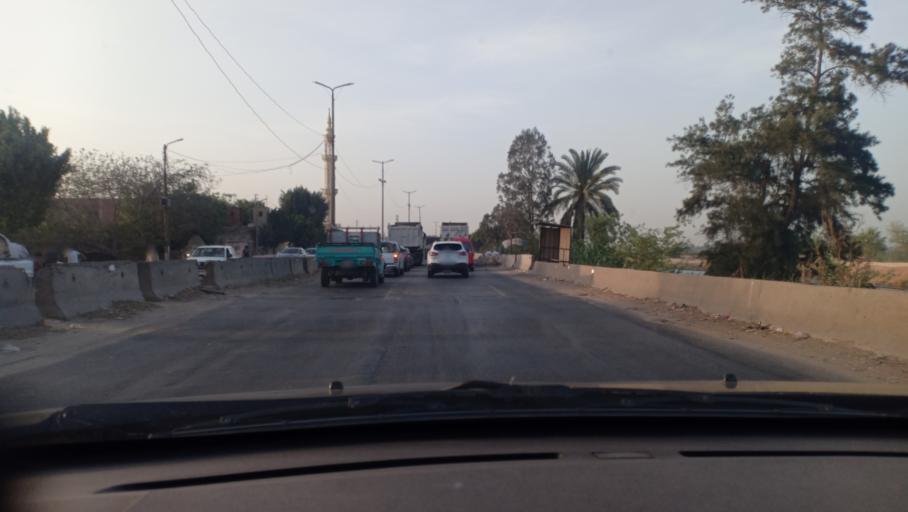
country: EG
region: Muhafazat al Minufiyah
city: Quwaysina
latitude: 30.5889
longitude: 31.2736
